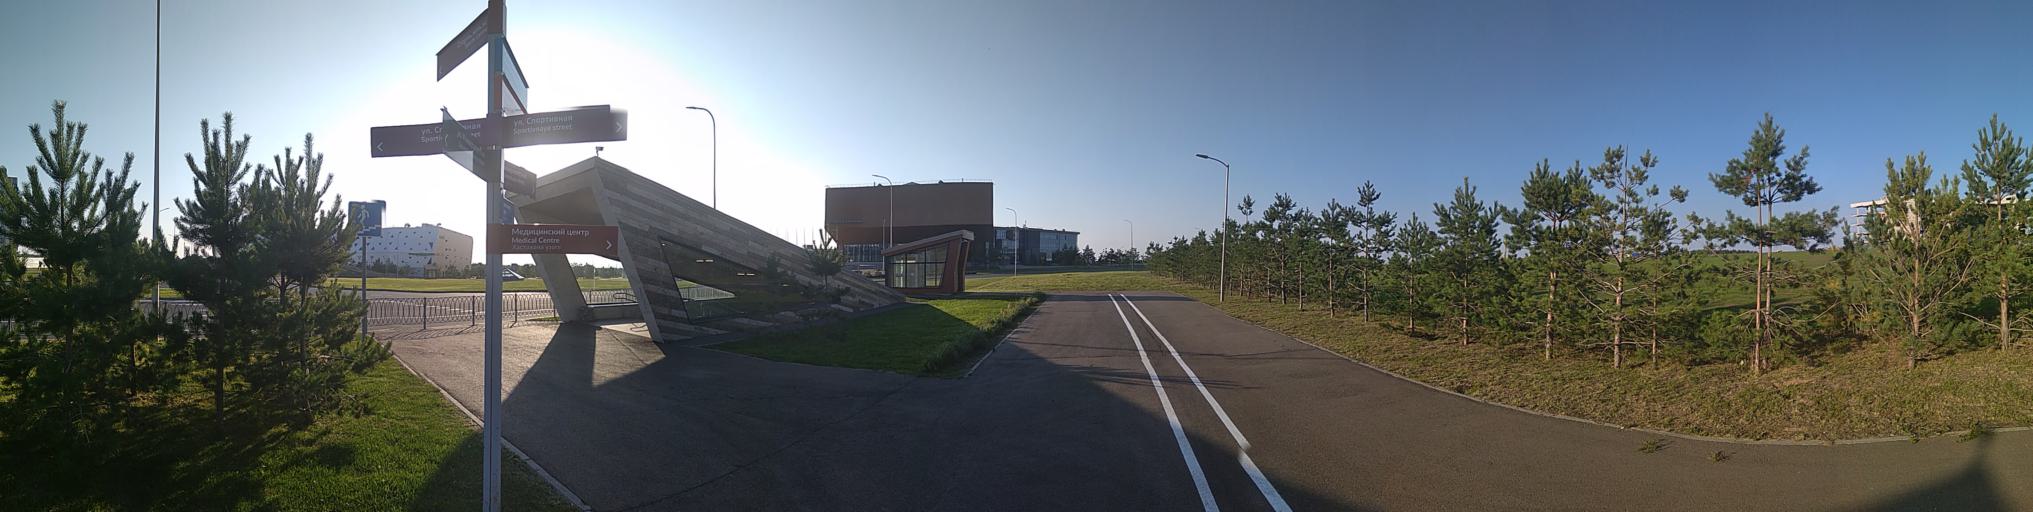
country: RU
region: Tatarstan
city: Sviyazhsk
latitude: 55.7499
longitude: 48.7456
